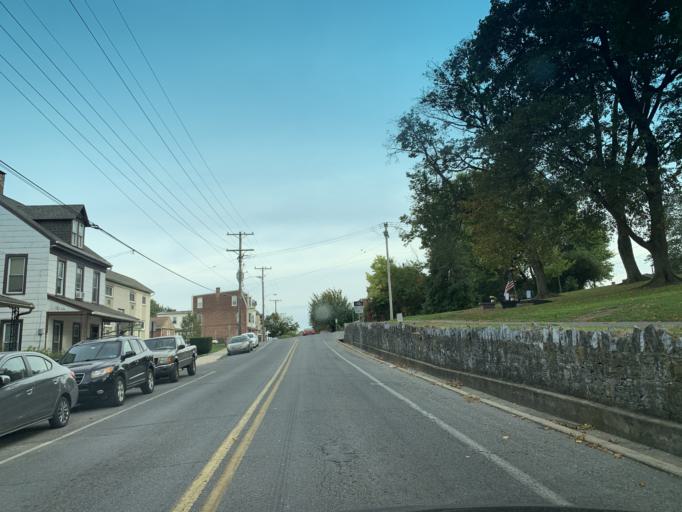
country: US
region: Pennsylvania
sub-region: York County
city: York
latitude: 39.9658
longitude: -76.7384
